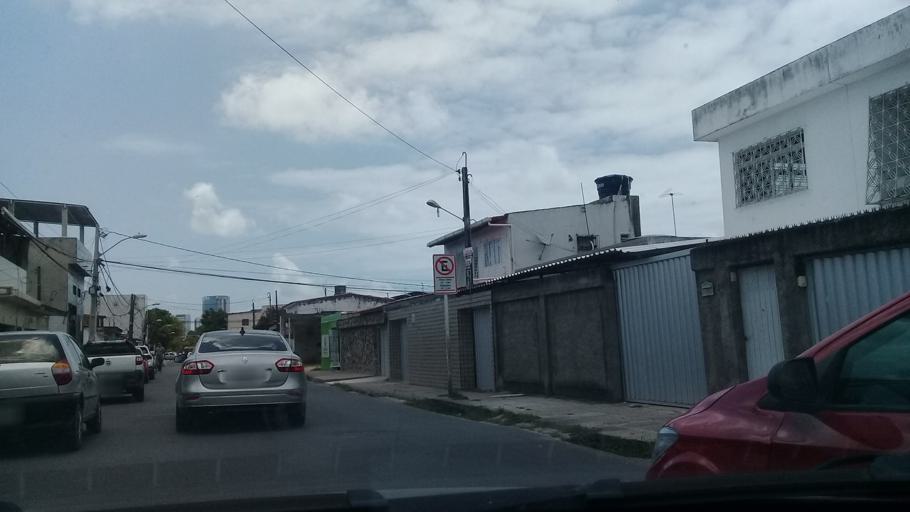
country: BR
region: Pernambuco
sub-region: Recife
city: Recife
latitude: -8.1069
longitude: -34.9182
